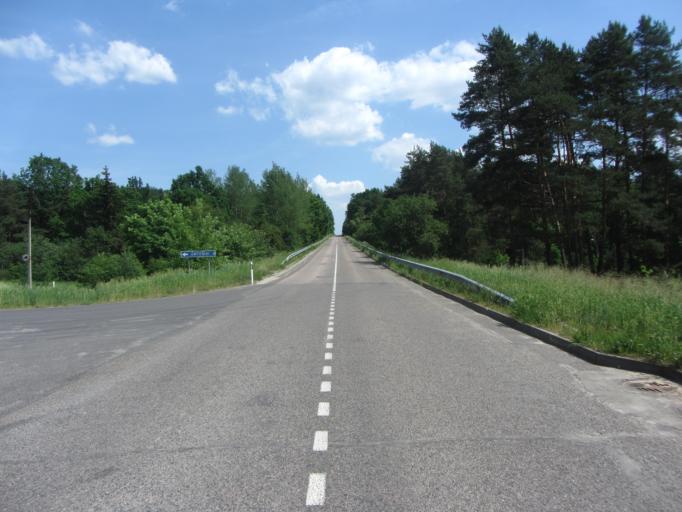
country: LT
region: Kauno apskritis
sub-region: Kauno rajonas
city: Karmelava
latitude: 54.9855
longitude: 24.0994
